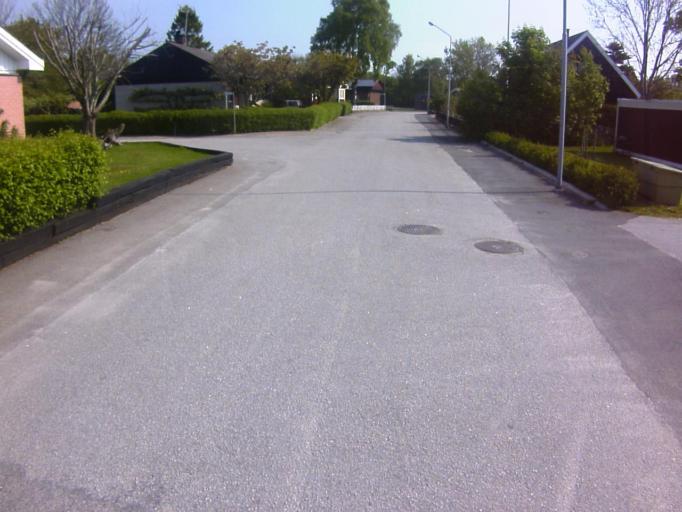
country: SE
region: Blekinge
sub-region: Solvesborgs Kommun
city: Soelvesborg
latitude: 56.0061
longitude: 14.7311
